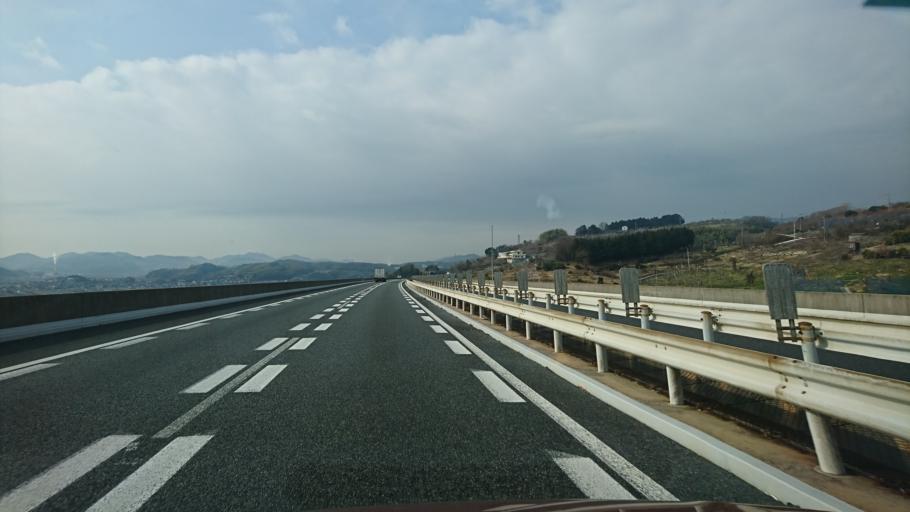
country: JP
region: Okayama
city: Kamogatacho-kamogata
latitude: 34.5703
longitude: 133.6653
